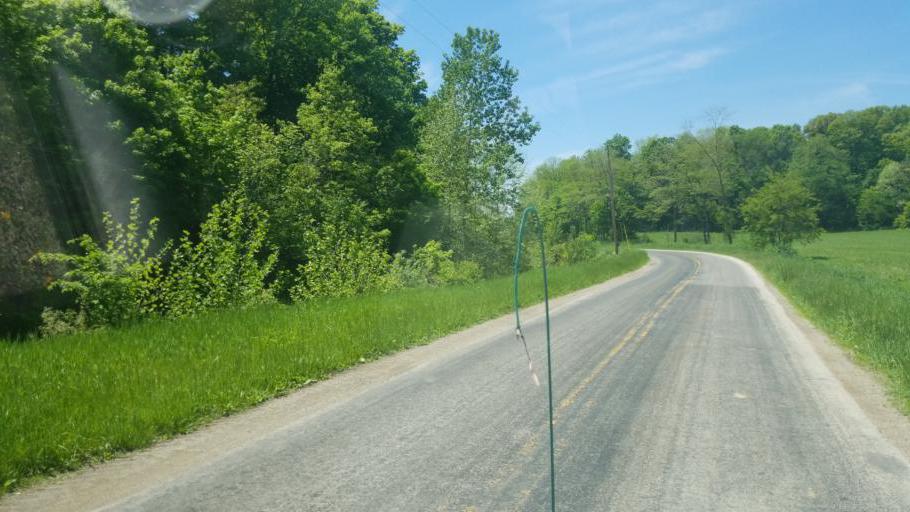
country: US
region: Ohio
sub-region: Huron County
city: New London
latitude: 40.9677
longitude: -82.3999
